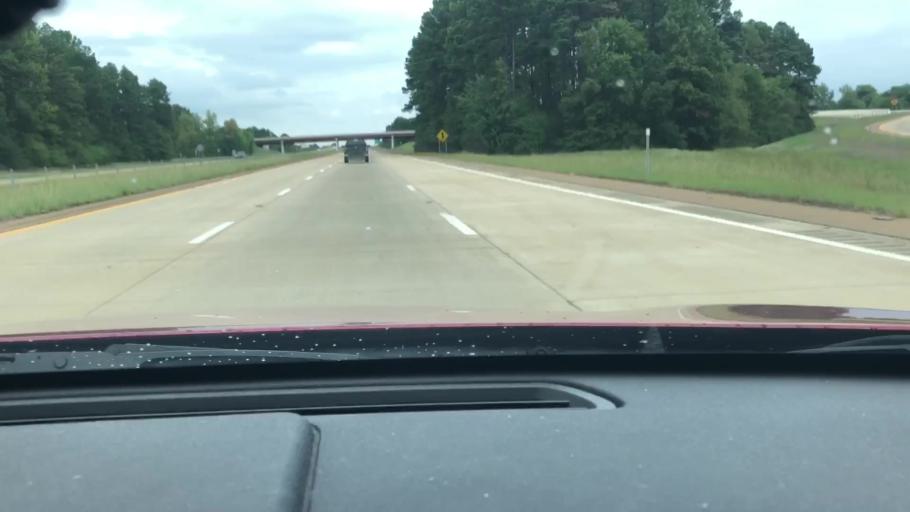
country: US
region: Texas
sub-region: Bowie County
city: Texarkana
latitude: 33.4086
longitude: -94.0048
